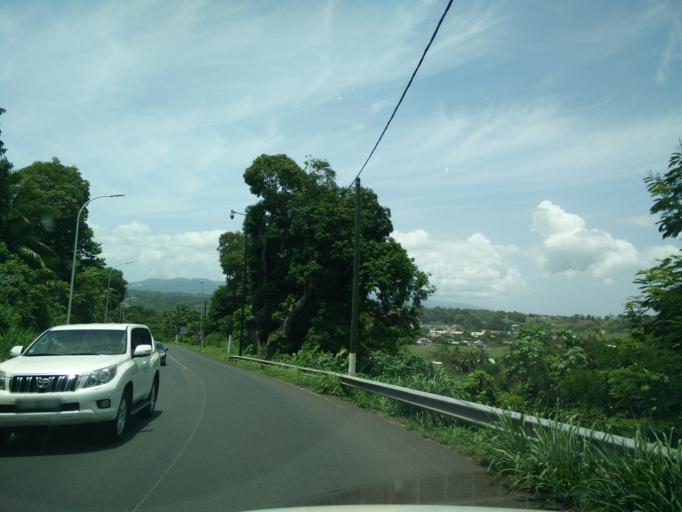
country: GP
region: Guadeloupe
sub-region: Guadeloupe
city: Petit-Bourg
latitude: 16.1980
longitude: -61.5971
